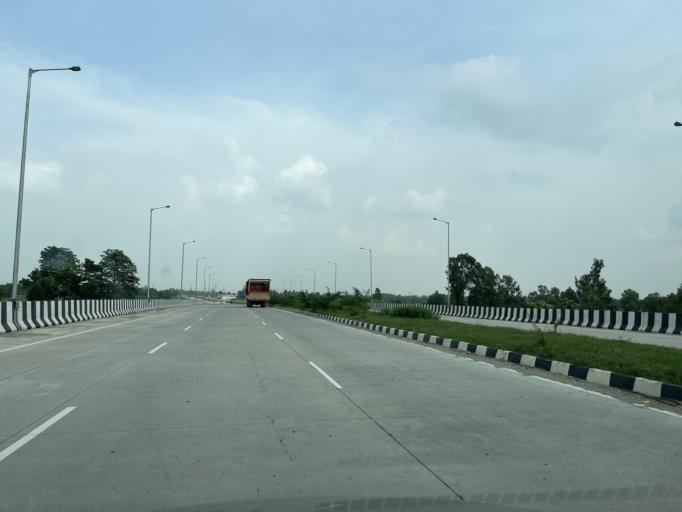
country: IN
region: Uttarakhand
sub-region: Udham Singh Nagar
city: Bazpur
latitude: 29.1490
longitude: 79.0581
